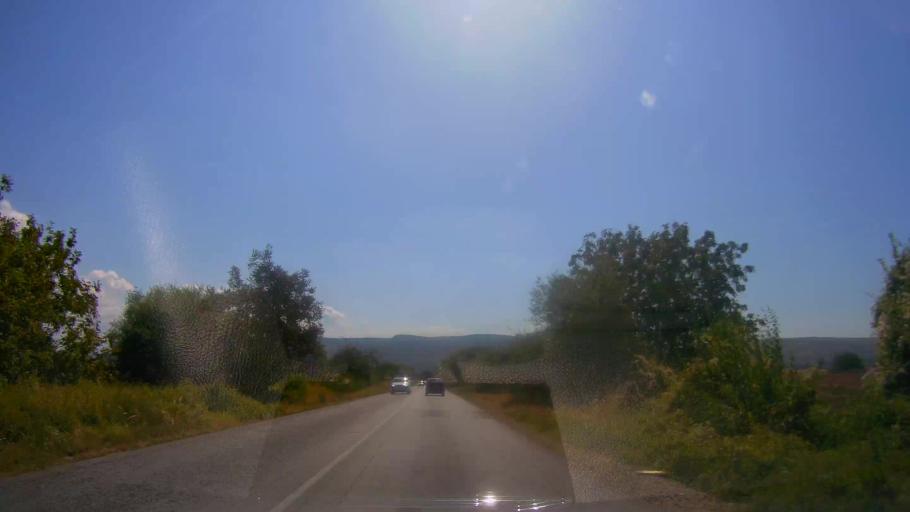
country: BG
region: Veliko Turnovo
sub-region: Obshtina Gorna Oryakhovitsa
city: Purvomaytsi
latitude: 43.1643
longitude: 25.6181
